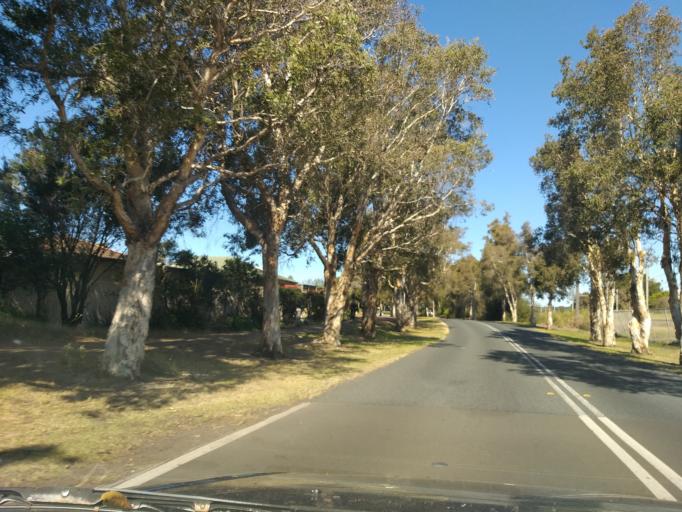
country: AU
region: New South Wales
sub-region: Wollongong
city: Bulli
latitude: -34.3550
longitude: 150.9134
